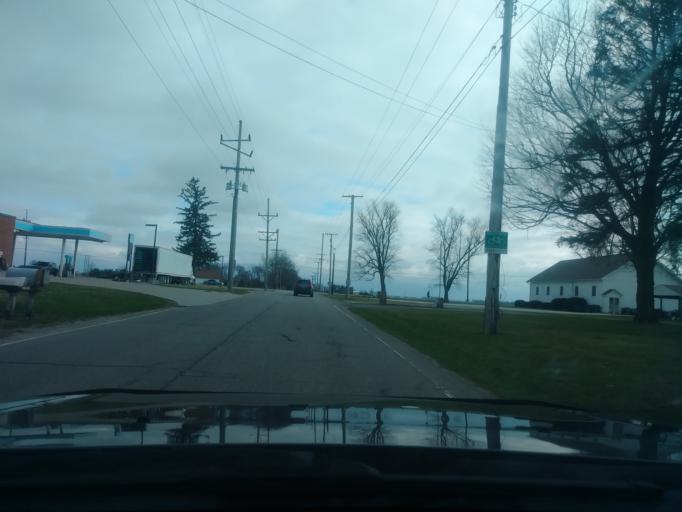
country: US
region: Indiana
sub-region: LaPorte County
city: LaPorte
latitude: 41.5928
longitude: -86.7979
